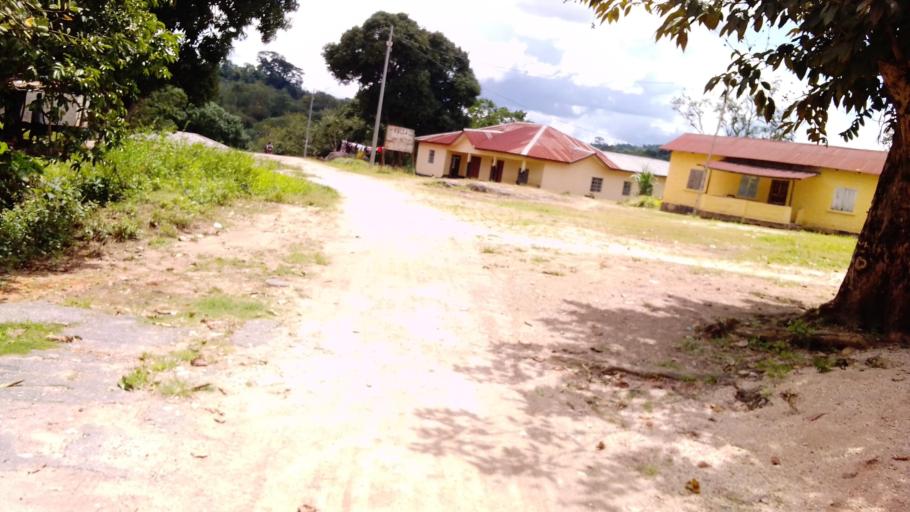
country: SL
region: Eastern Province
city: Koyima
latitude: 8.7007
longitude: -11.0121
